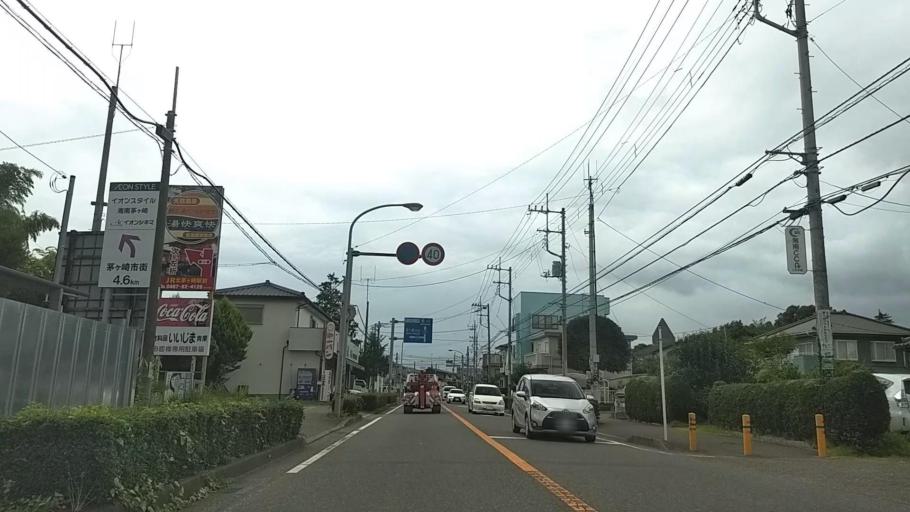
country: JP
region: Kanagawa
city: Chigasaki
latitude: 35.3706
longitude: 139.4266
